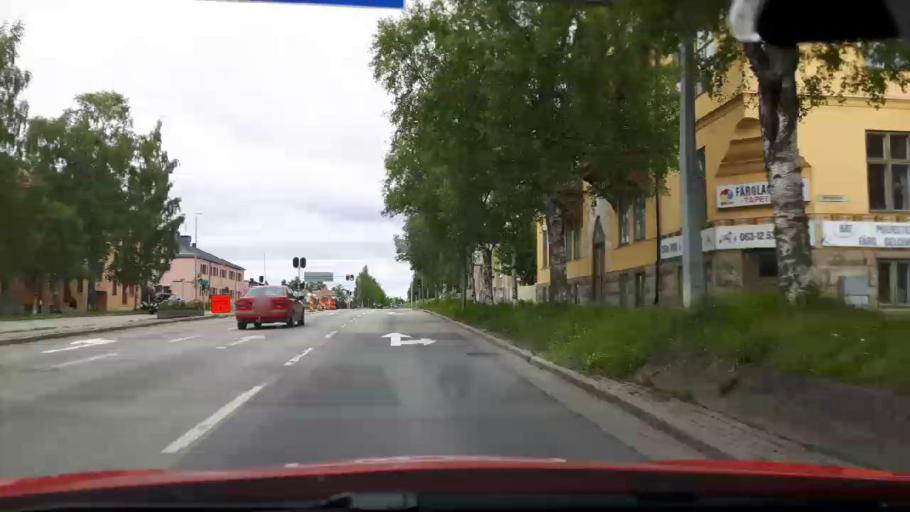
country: SE
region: Jaemtland
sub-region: OEstersunds Kommun
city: Ostersund
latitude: 63.1814
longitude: 14.6400
